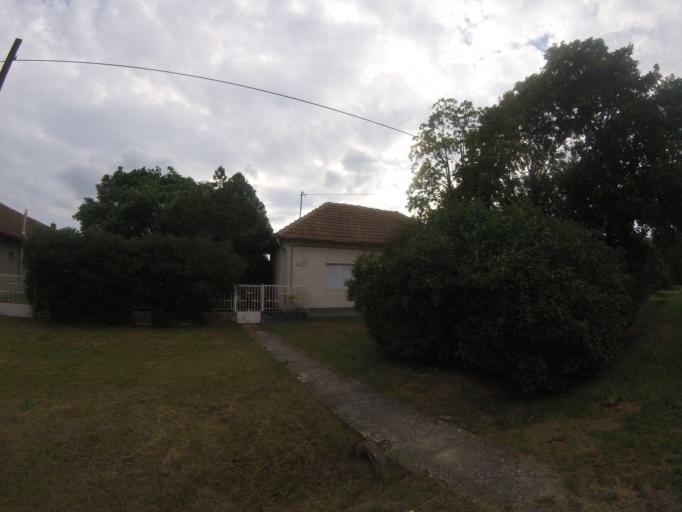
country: HU
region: Heves
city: Tiszanana
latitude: 47.5874
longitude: 20.5973
